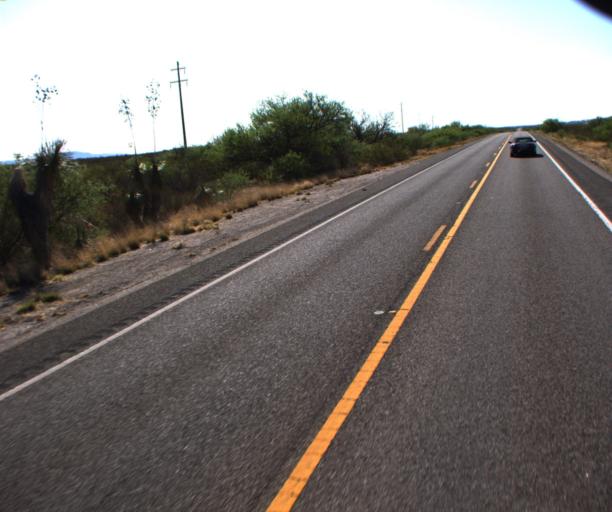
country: US
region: Arizona
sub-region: Cochise County
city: Tombstone
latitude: 31.7641
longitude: -110.1164
